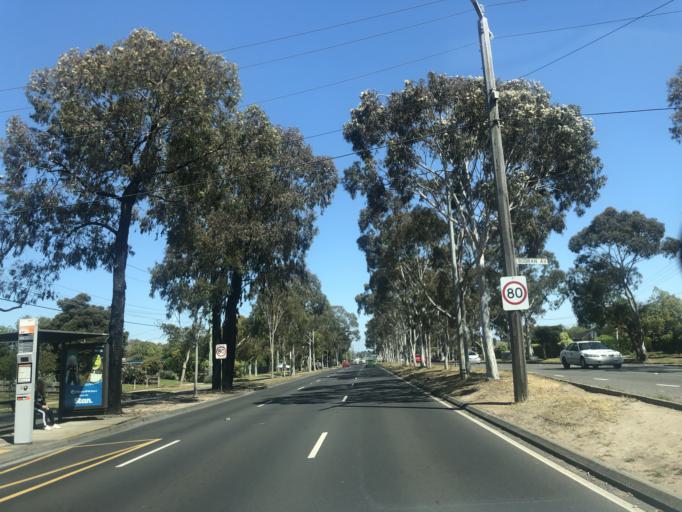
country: AU
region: Victoria
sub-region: Monash
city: Notting Hill
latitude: -37.8982
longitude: 145.1634
